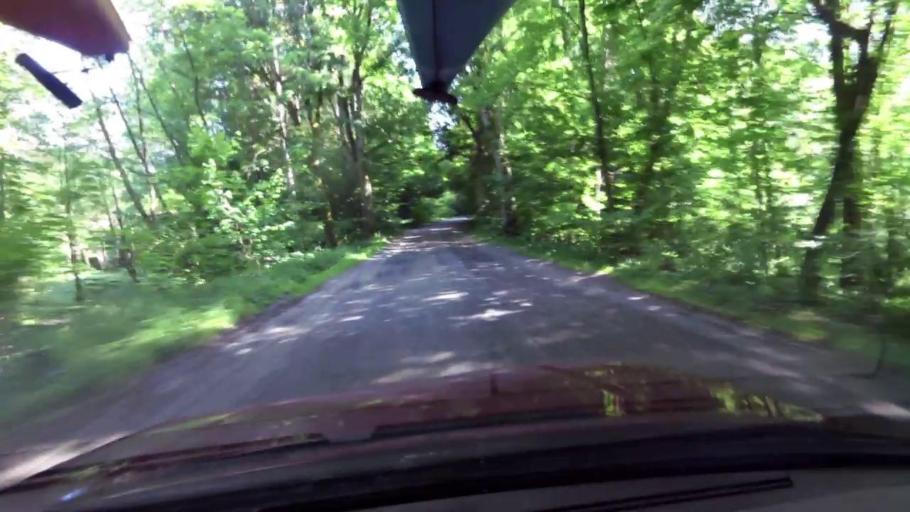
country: PL
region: Pomeranian Voivodeship
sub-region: Powiat slupski
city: Kepice
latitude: 54.1624
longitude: 16.9070
